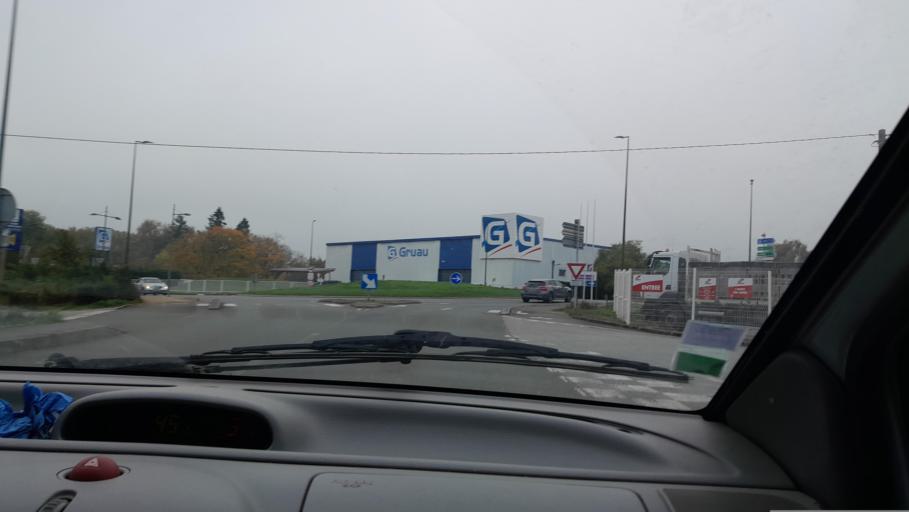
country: FR
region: Pays de la Loire
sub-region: Departement de la Mayenne
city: Saint-Berthevin
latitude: 48.0681
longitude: -0.8134
